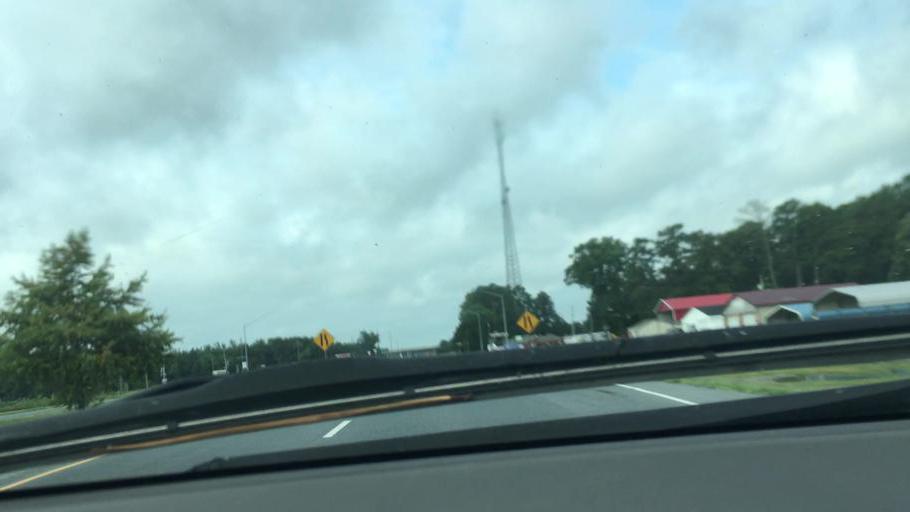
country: US
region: Maryland
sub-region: Wicomico County
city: Fruitland
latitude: 38.3086
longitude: -75.6298
